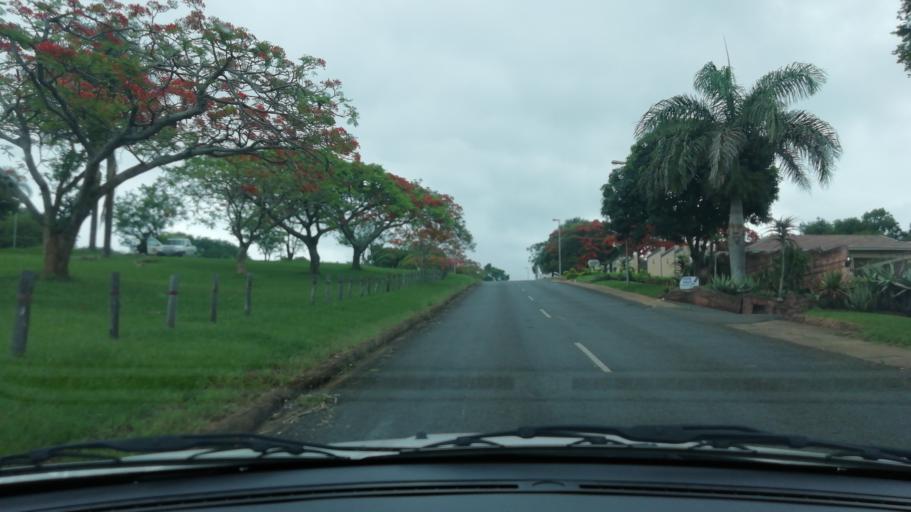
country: ZA
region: KwaZulu-Natal
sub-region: uThungulu District Municipality
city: Empangeni
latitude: -28.7616
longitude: 31.8919
